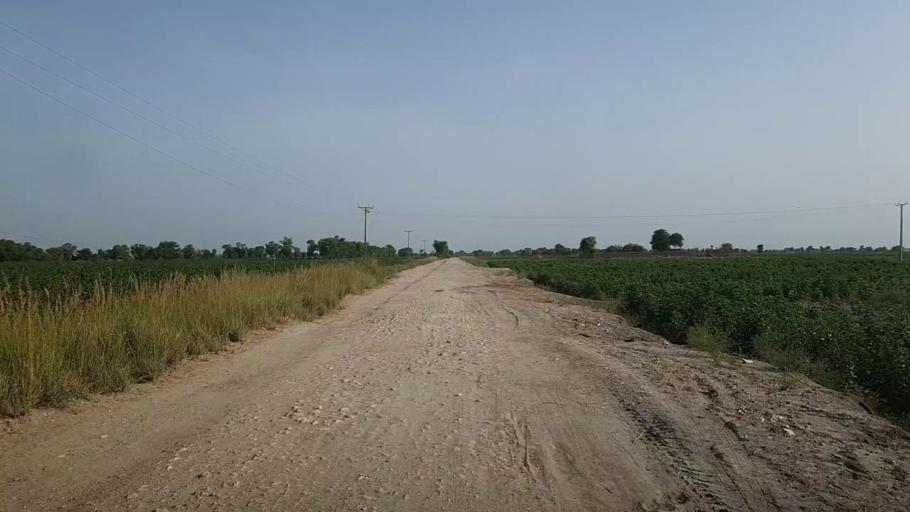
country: PK
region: Sindh
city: Pad Idan
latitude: 26.7659
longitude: 68.2572
